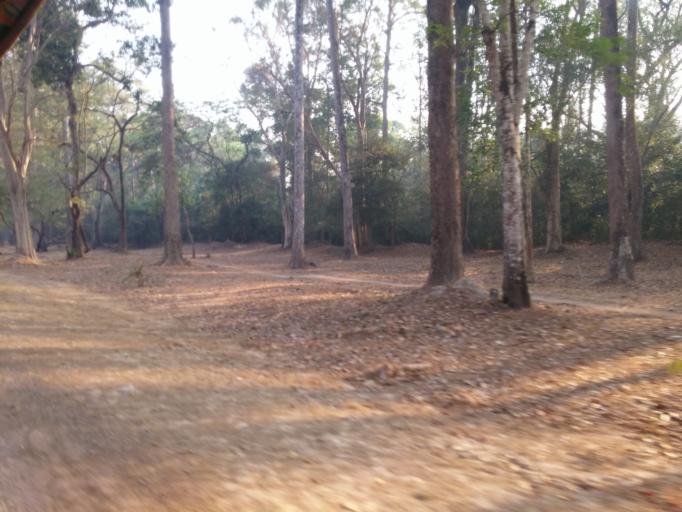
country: KH
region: Siem Reap
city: Siem Reap
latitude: 13.4359
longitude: 103.8594
